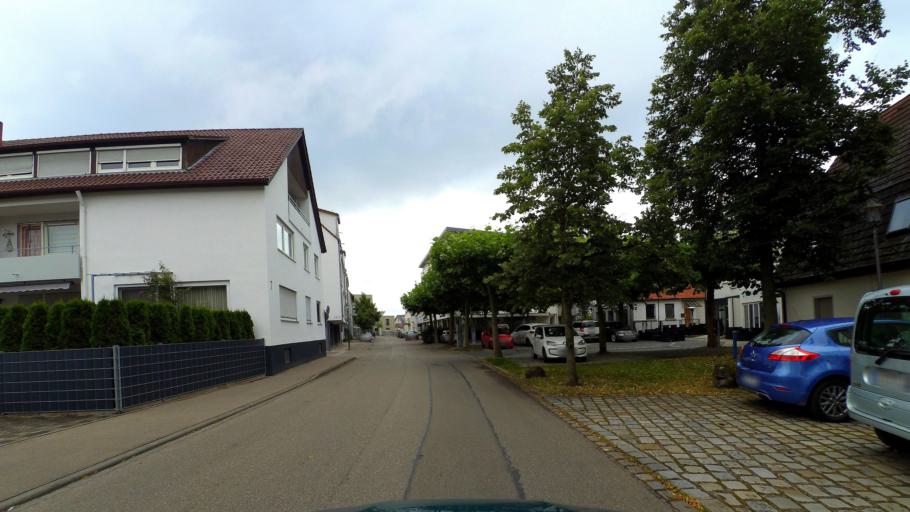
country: DE
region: Baden-Wuerttemberg
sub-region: Tuebingen Region
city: Langenau
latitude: 48.4975
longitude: 10.1211
